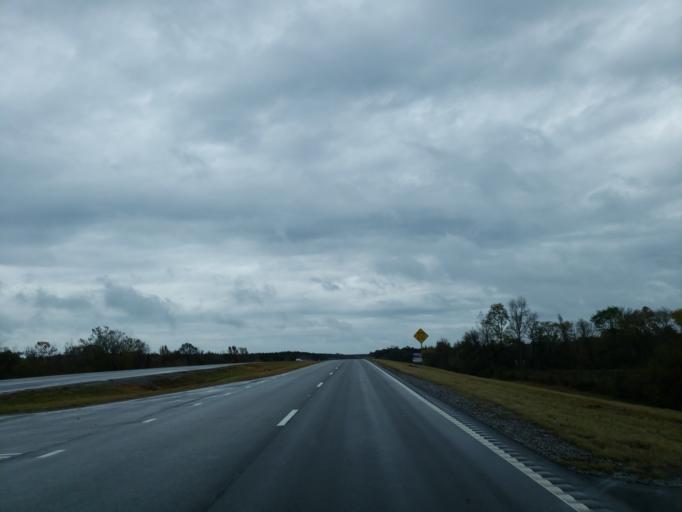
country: US
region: Mississippi
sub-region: Wayne County
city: Waynesboro
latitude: 31.6911
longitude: -88.6661
